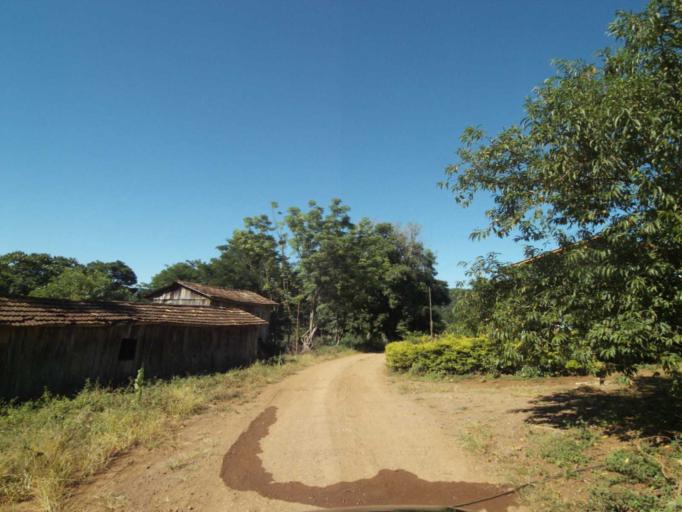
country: BR
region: Parana
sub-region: Francisco Beltrao
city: Francisco Beltrao
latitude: -26.1411
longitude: -53.3105
